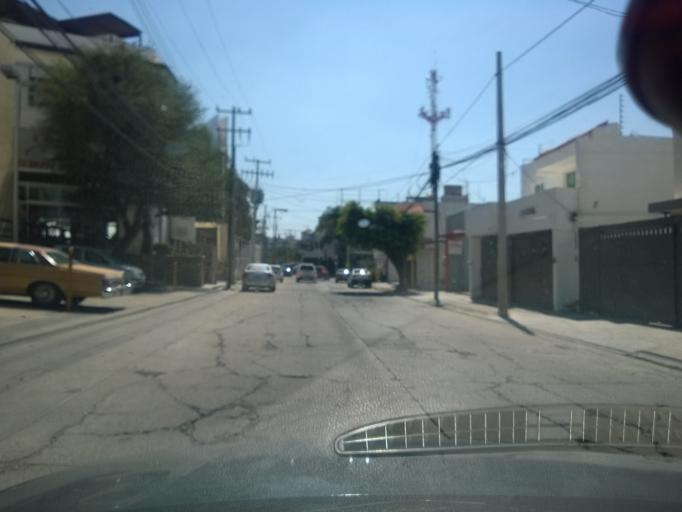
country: MX
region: Guanajuato
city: Leon
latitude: 21.1535
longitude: -101.6895
